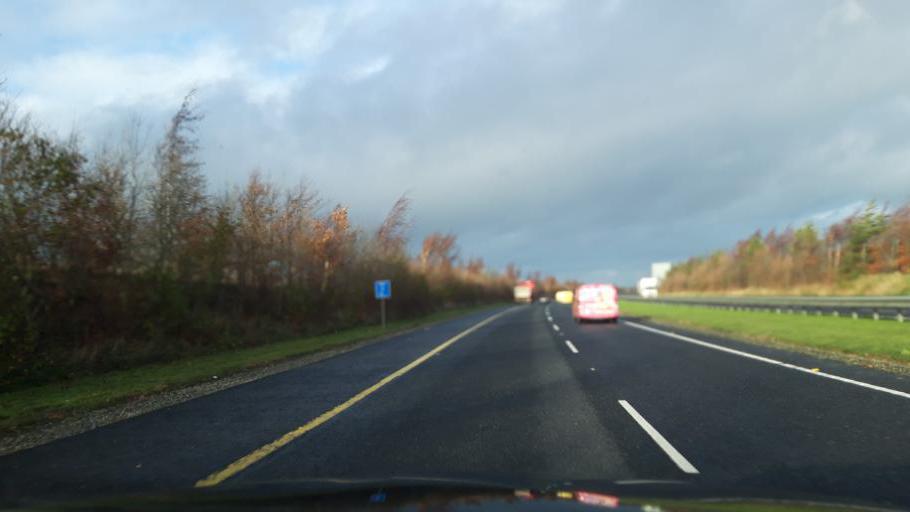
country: IE
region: Leinster
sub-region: Fingal County
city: Blanchardstown
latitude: 53.4410
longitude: -6.3554
